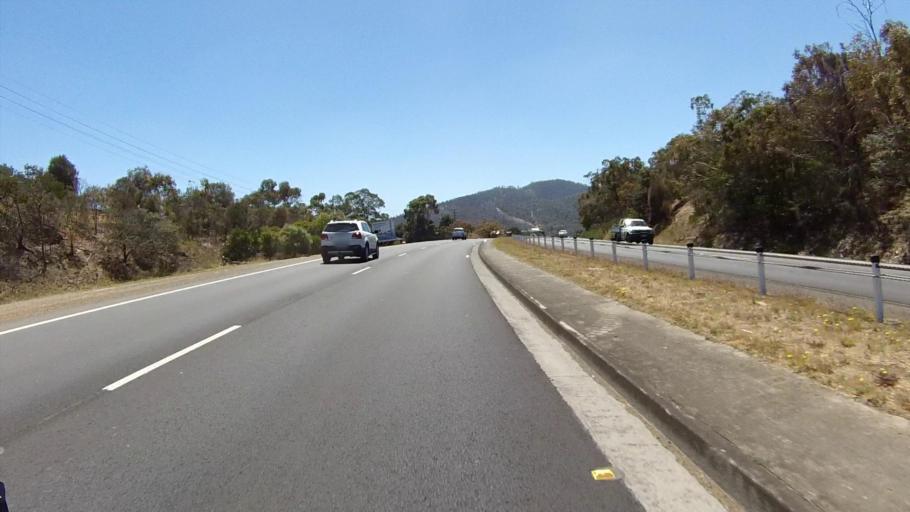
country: AU
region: Tasmania
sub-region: Clarence
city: Warrane
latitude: -42.8654
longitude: 147.3936
